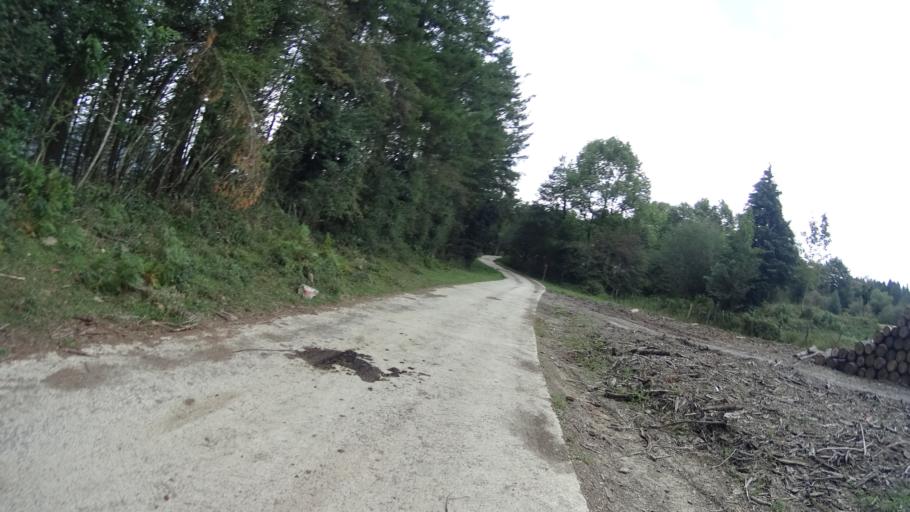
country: ES
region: Basque Country
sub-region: Bizkaia
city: Zeanuri
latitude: 43.0519
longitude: -2.7305
